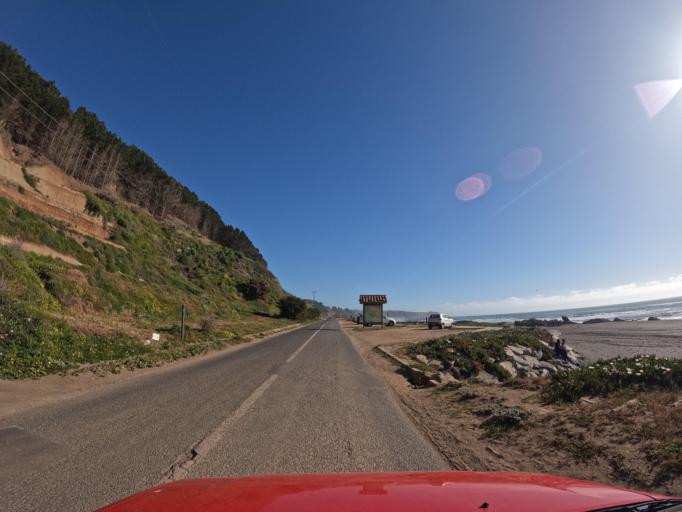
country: CL
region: Maule
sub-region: Provincia de Talca
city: Constitucion
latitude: -34.8606
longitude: -72.1468
